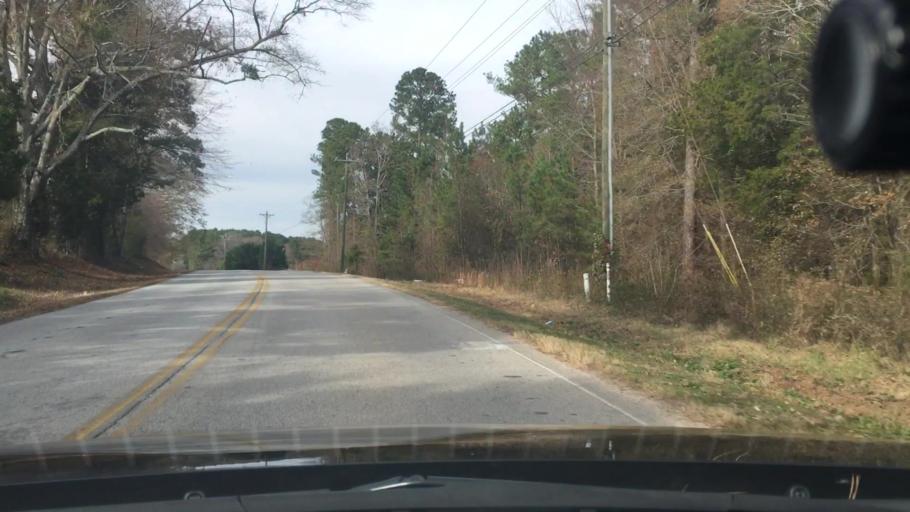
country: US
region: Georgia
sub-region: Coweta County
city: Senoia
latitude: 33.2995
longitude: -84.4614
